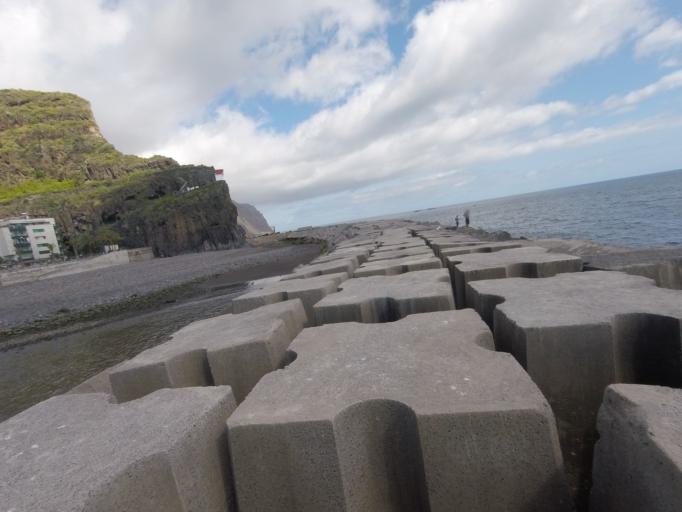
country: PT
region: Madeira
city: Ribeira Brava
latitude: 32.6691
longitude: -17.0662
